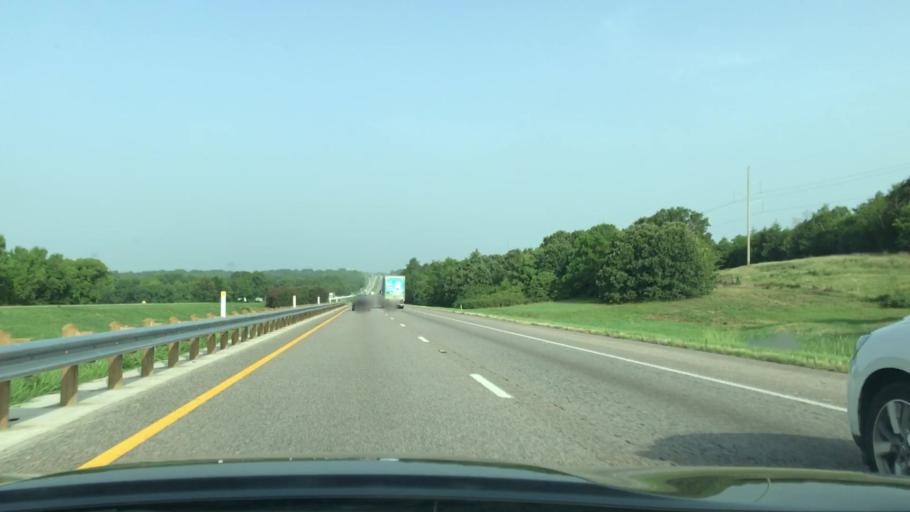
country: US
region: Texas
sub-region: Smith County
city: Hideaway
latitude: 32.4811
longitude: -95.4951
